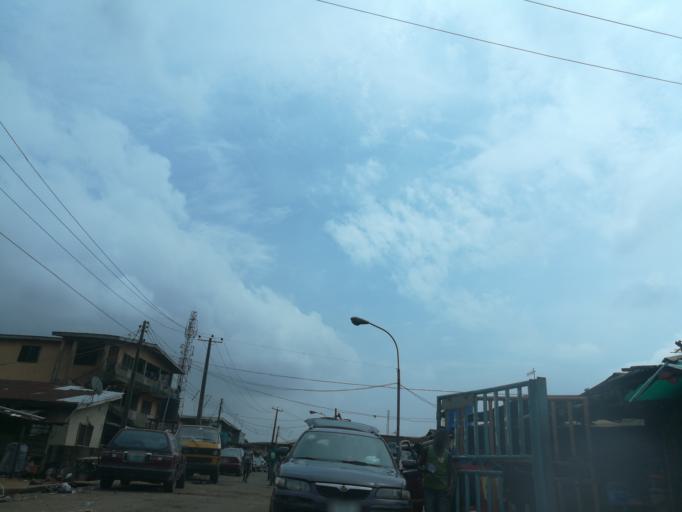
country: NG
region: Lagos
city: Ojota
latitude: 6.5698
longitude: 3.3631
